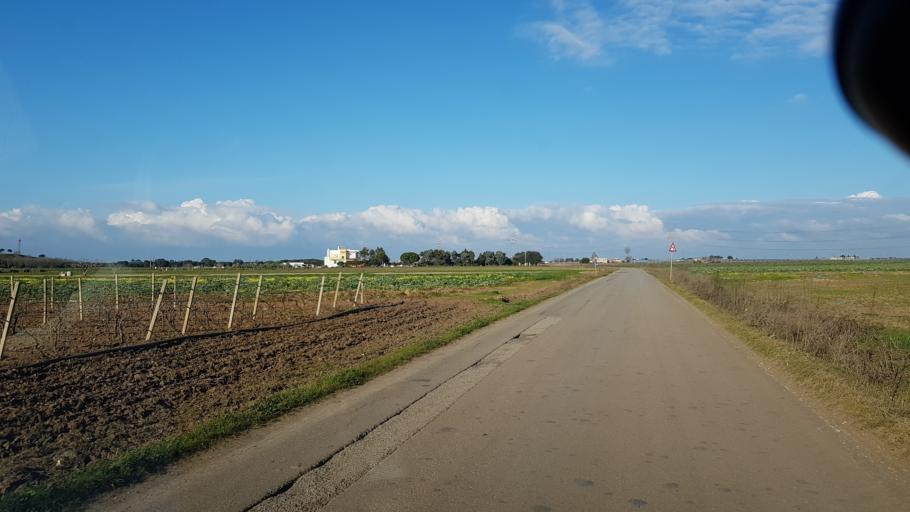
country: IT
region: Apulia
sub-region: Provincia di Brindisi
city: Tuturano
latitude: 40.5761
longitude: 17.9005
